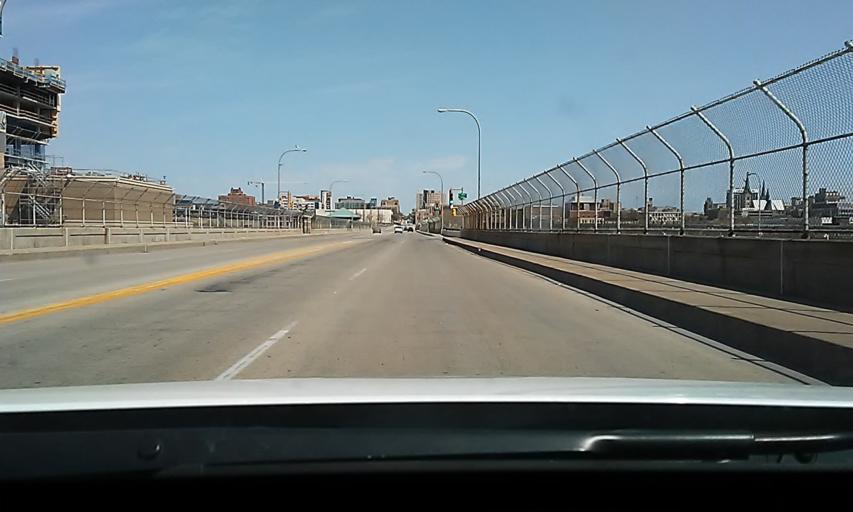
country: US
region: Wisconsin
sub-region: Milwaukee County
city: Milwaukee
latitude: 43.0297
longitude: -87.9331
